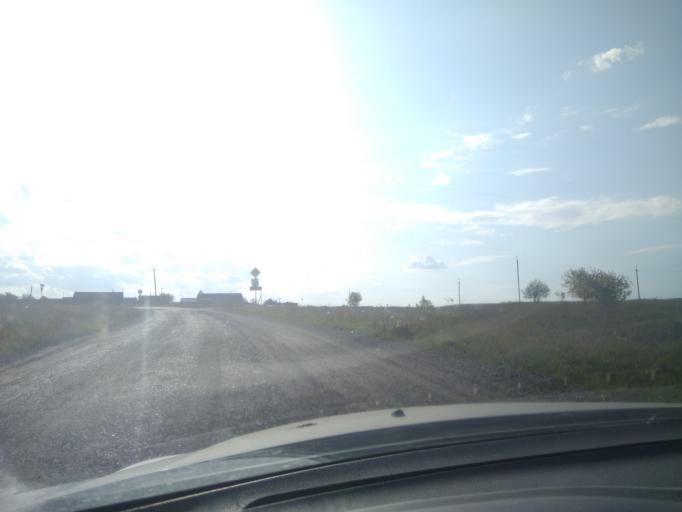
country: RU
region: Sverdlovsk
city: Pokrovskoye
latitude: 56.4366
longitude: 61.5886
